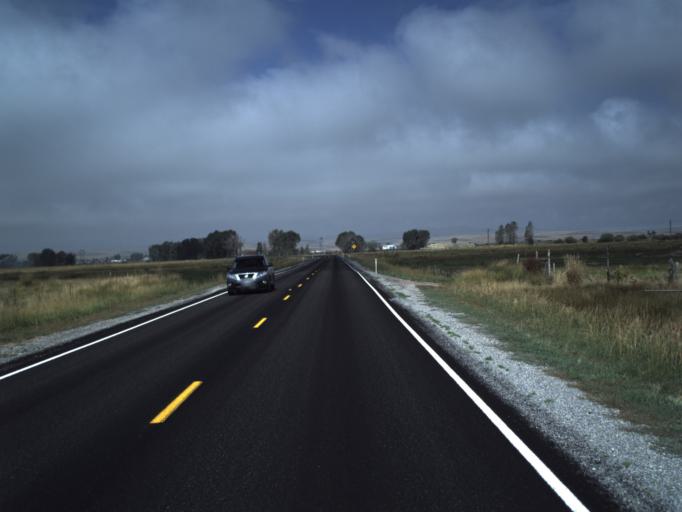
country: US
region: Utah
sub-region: Rich County
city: Randolph
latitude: 41.5140
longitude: -111.1350
